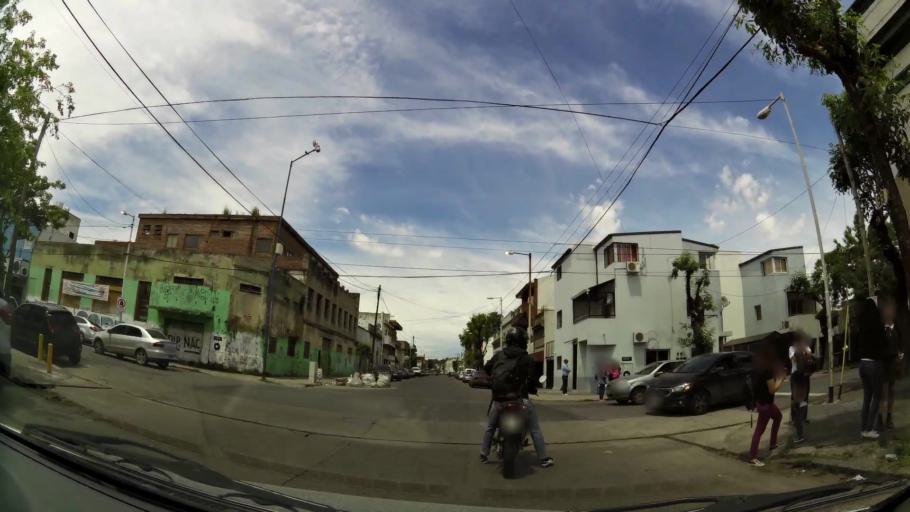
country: AR
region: Buenos Aires
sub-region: Partido de Avellaneda
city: Avellaneda
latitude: -34.6644
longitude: -58.3813
